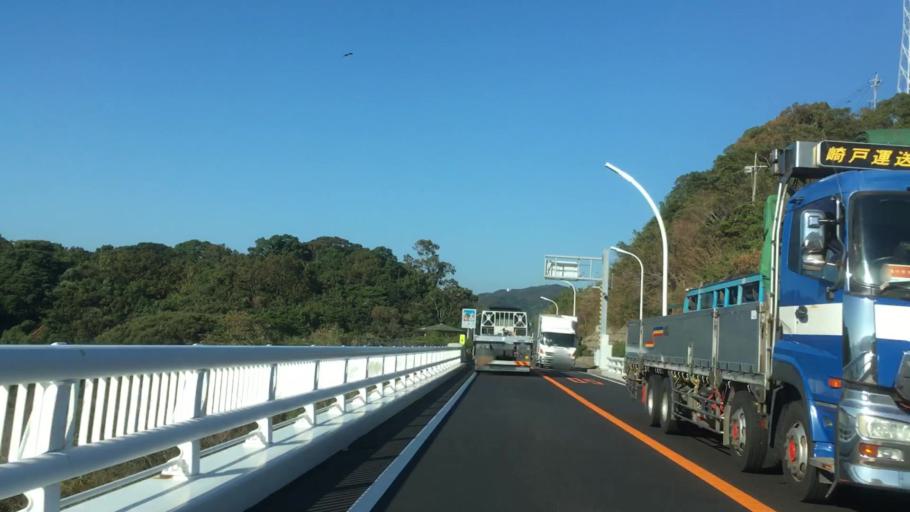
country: JP
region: Nagasaki
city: Sasebo
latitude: 33.0378
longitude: 129.6373
